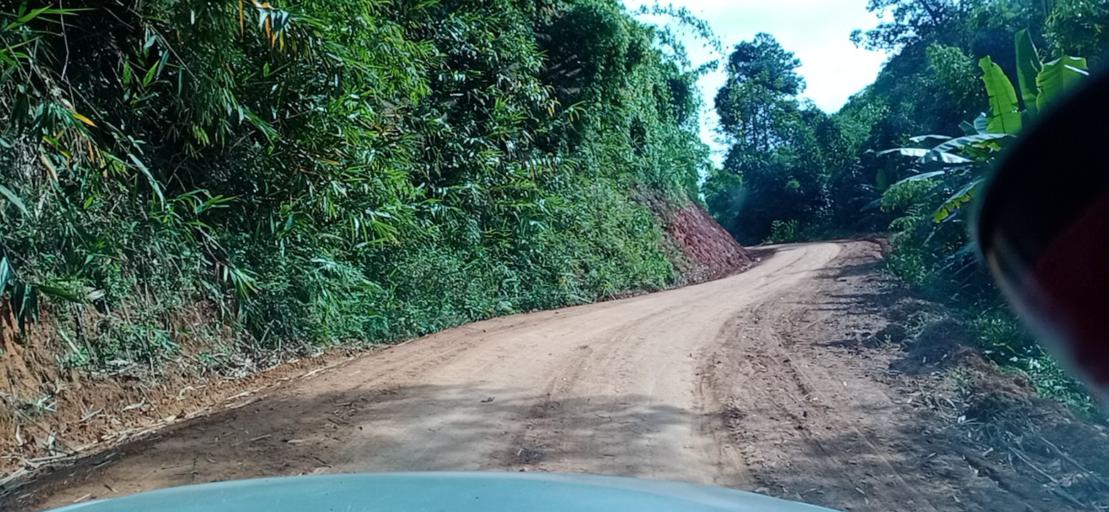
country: TH
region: Changwat Bueng Kan
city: Pak Khat
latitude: 18.6382
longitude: 103.2397
